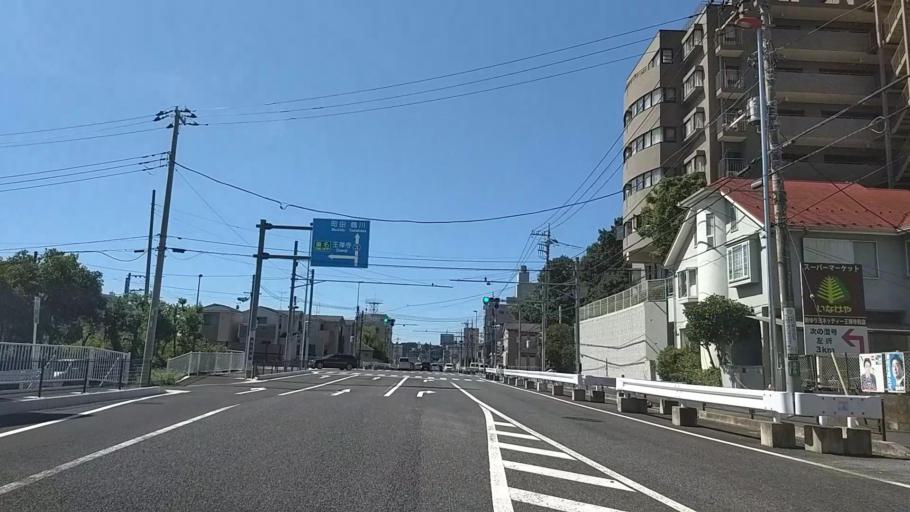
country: JP
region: Tokyo
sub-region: Machida-shi
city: Machida
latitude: 35.5938
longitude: 139.4984
